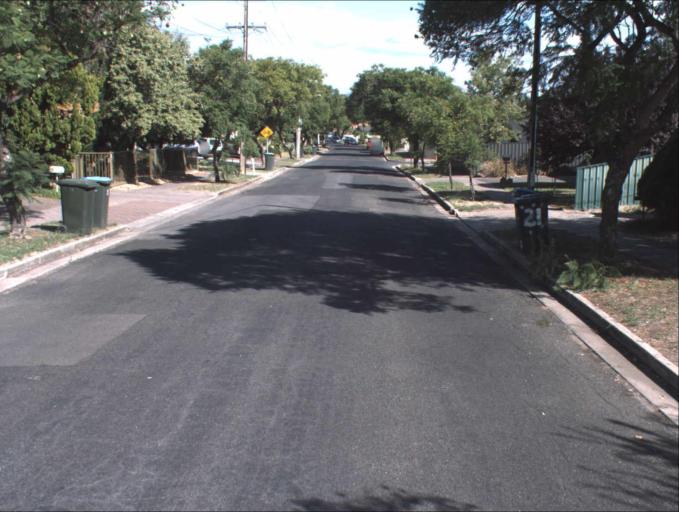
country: AU
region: South Australia
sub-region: Port Adelaide Enfield
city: Gilles Plains
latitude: -34.8637
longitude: 138.6411
